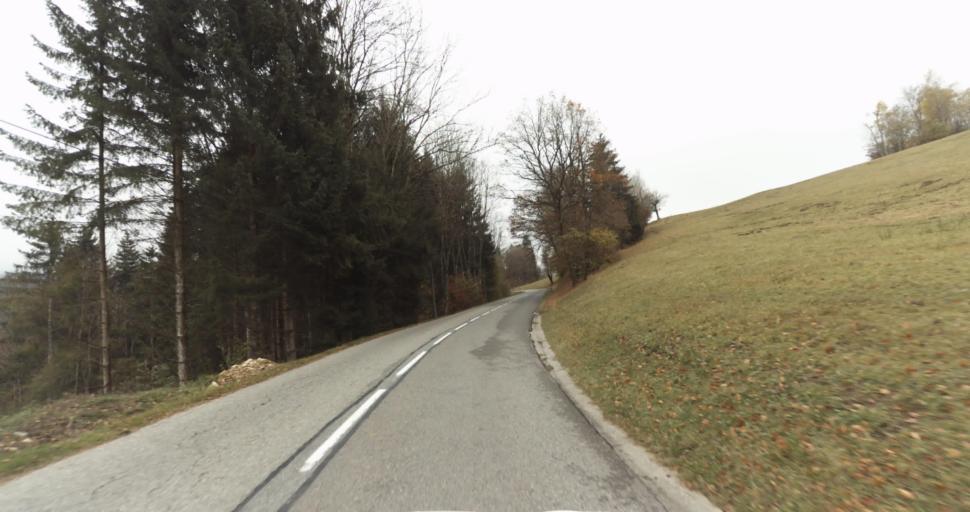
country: FR
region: Rhone-Alpes
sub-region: Departement de la Haute-Savoie
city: Saint-Jorioz
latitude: 45.7769
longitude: 6.1328
